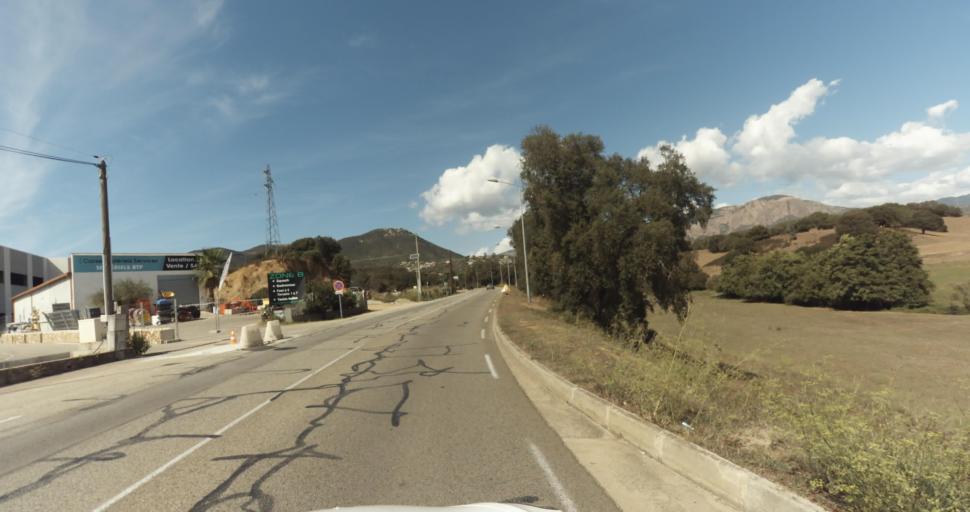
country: FR
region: Corsica
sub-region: Departement de la Corse-du-Sud
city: Afa
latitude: 41.9562
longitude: 8.7823
